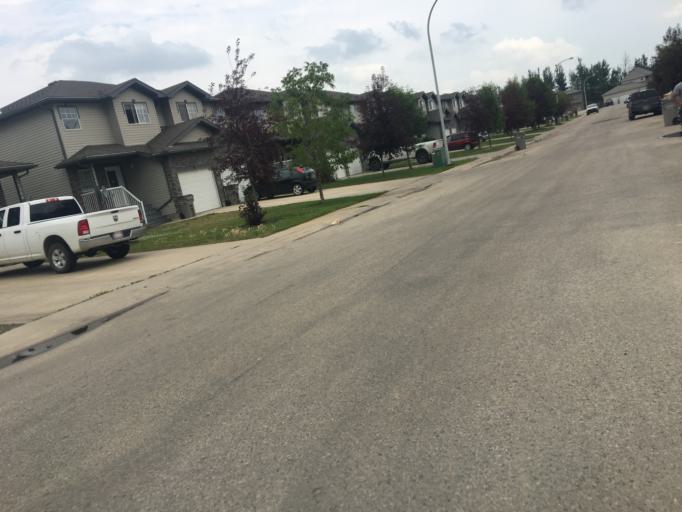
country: CA
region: Alberta
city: Grande Prairie
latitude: 55.1436
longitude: -118.8023
